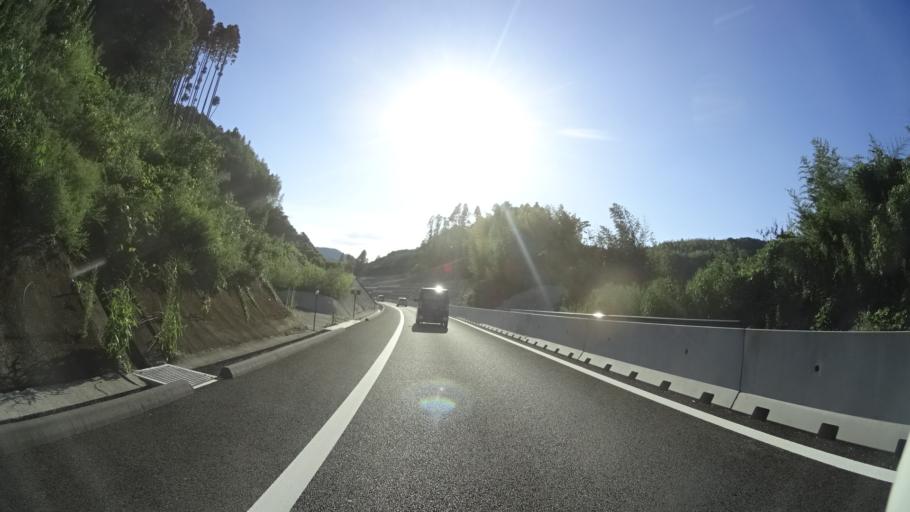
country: JP
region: Kumamoto
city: Ozu
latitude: 32.7526
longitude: 130.8559
